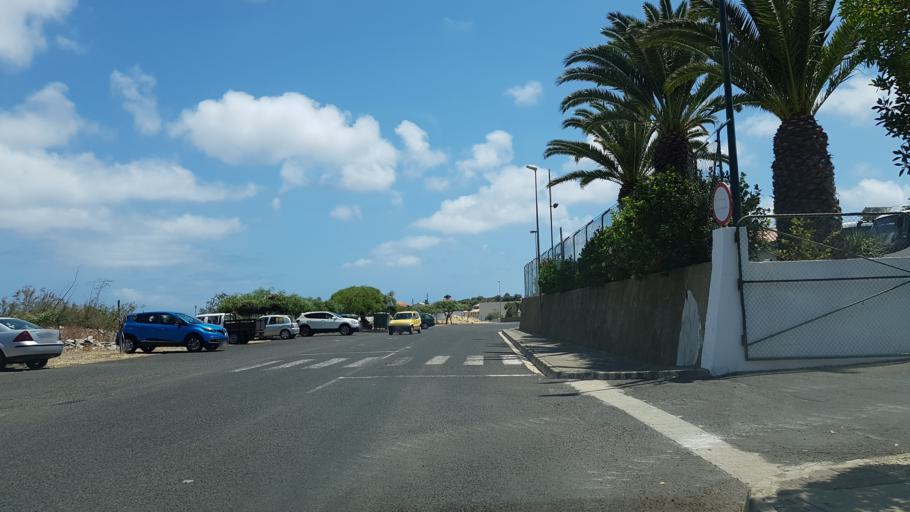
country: PT
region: Madeira
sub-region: Porto Santo
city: Vila de Porto Santo
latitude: 33.0703
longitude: -16.3426
